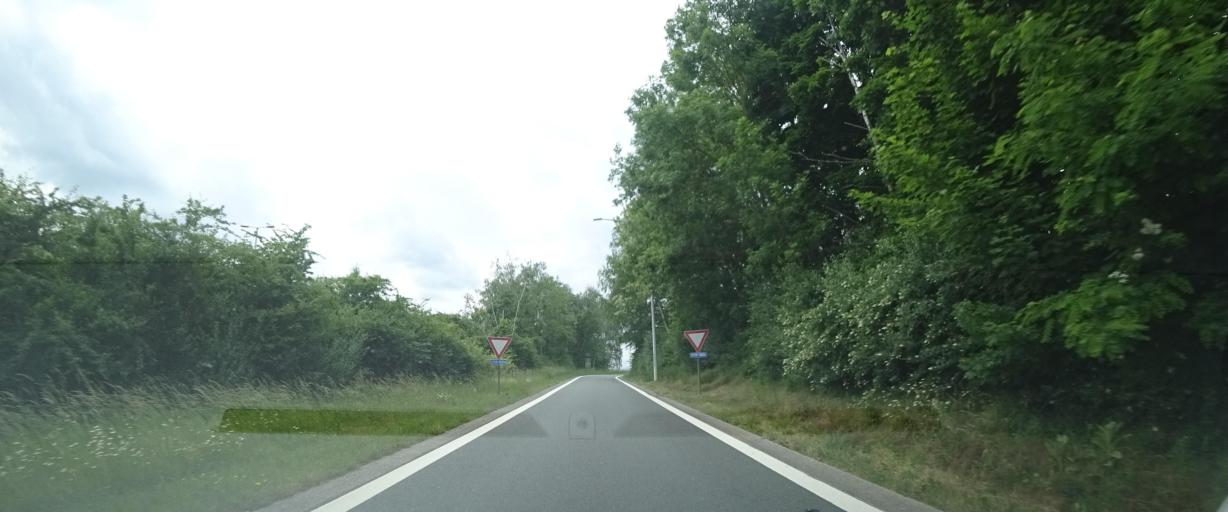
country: BE
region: Wallonia
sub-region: Province du Brabant Wallon
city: Court-Saint-Etienne
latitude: 50.6316
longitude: 4.5544
